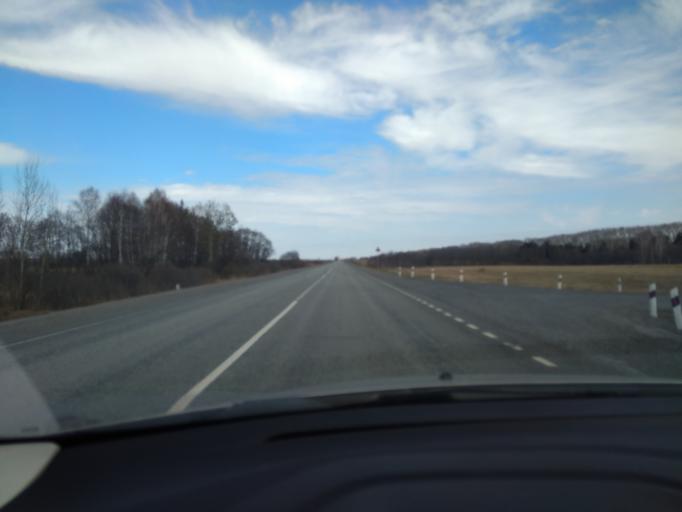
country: RU
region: Sverdlovsk
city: Pyshma
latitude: 57.0080
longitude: 63.3409
